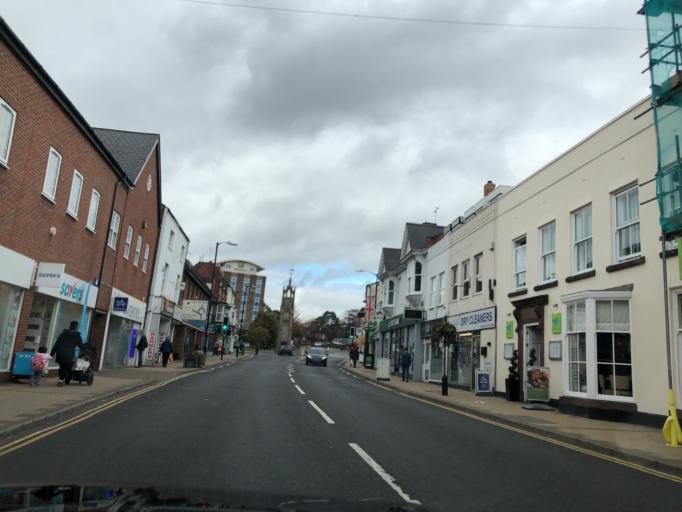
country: GB
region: England
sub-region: Warwickshire
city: Kenilworth
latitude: 52.3425
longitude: -1.5790
